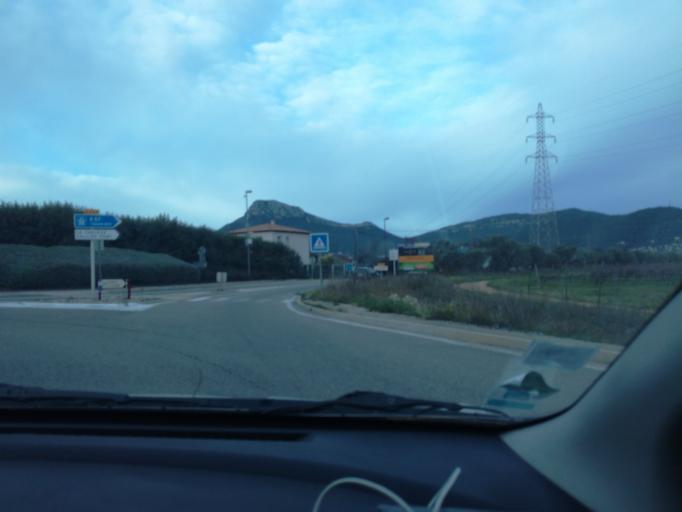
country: FR
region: Provence-Alpes-Cote d'Azur
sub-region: Departement du Var
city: La Crau
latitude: 43.1552
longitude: 6.0701
